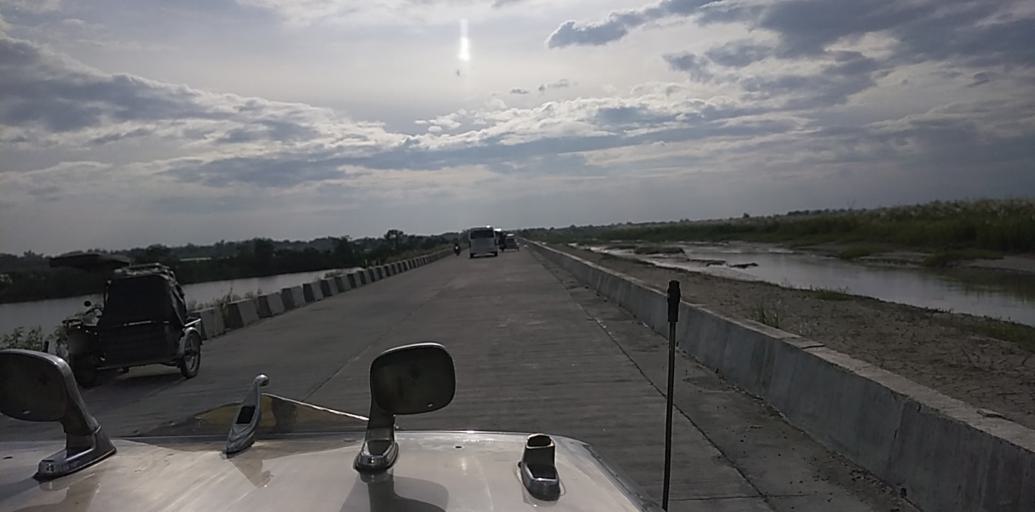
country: PH
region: Central Luzon
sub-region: Province of Pampanga
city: Minalin
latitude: 14.9700
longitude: 120.6767
